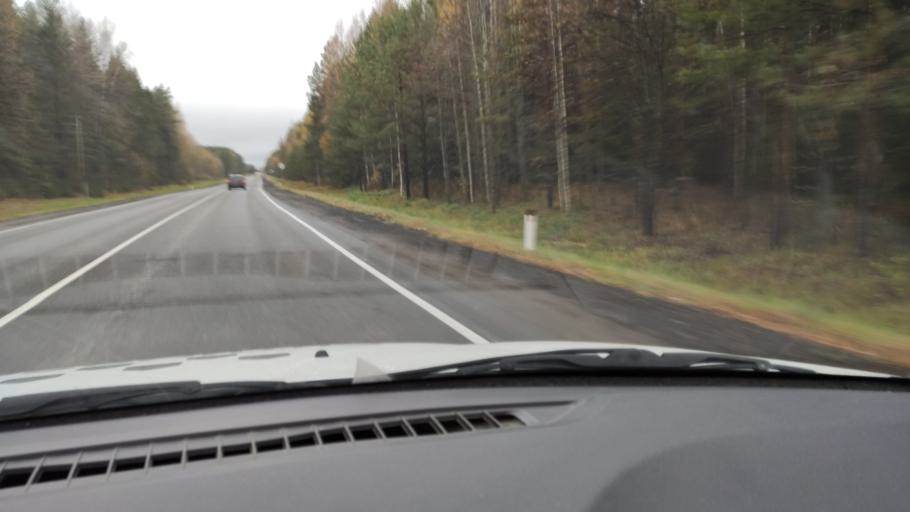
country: RU
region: Kirov
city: Belaya Kholunitsa
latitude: 58.8960
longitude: 50.9124
